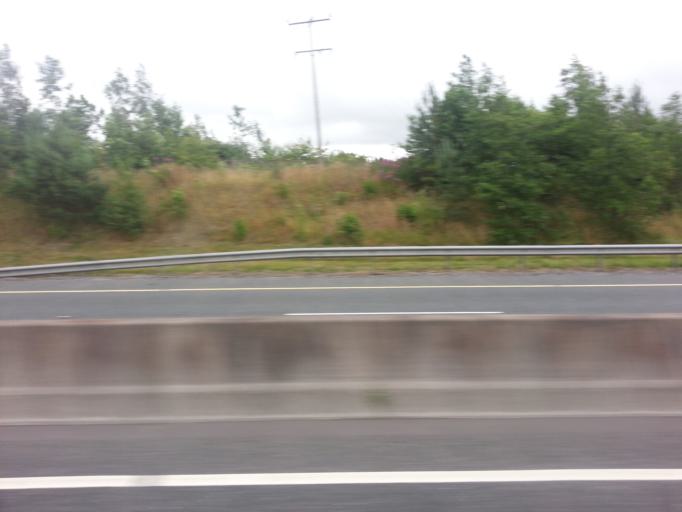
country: IE
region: Leinster
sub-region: Kildare
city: Castledermot
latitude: 52.8722
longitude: -6.8393
